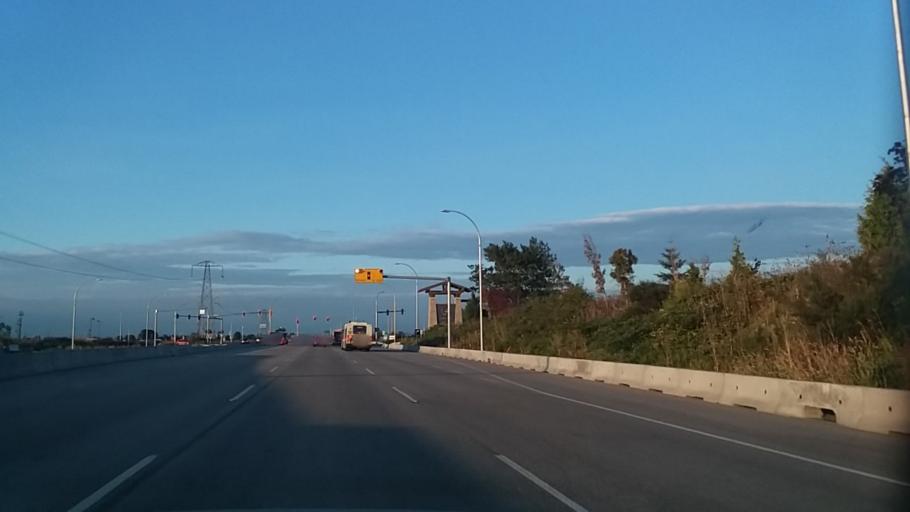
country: US
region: Washington
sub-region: Whatcom County
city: Point Roberts
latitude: 49.0365
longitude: -123.0819
